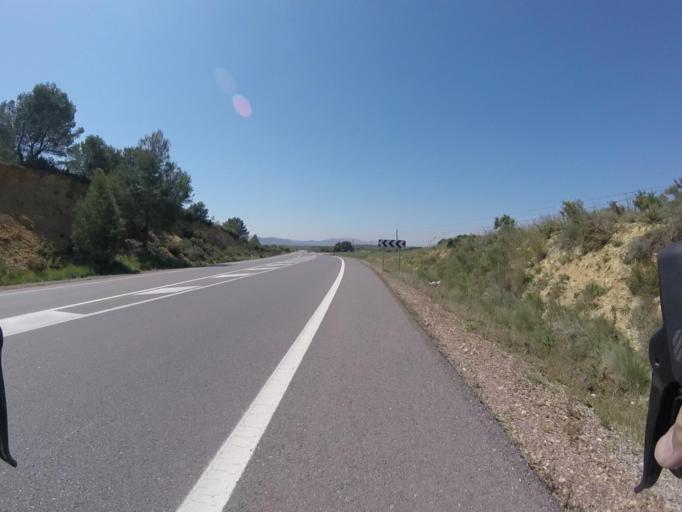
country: ES
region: Valencia
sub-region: Provincia de Castello
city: Benlloch
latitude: 40.2201
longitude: 0.0474
